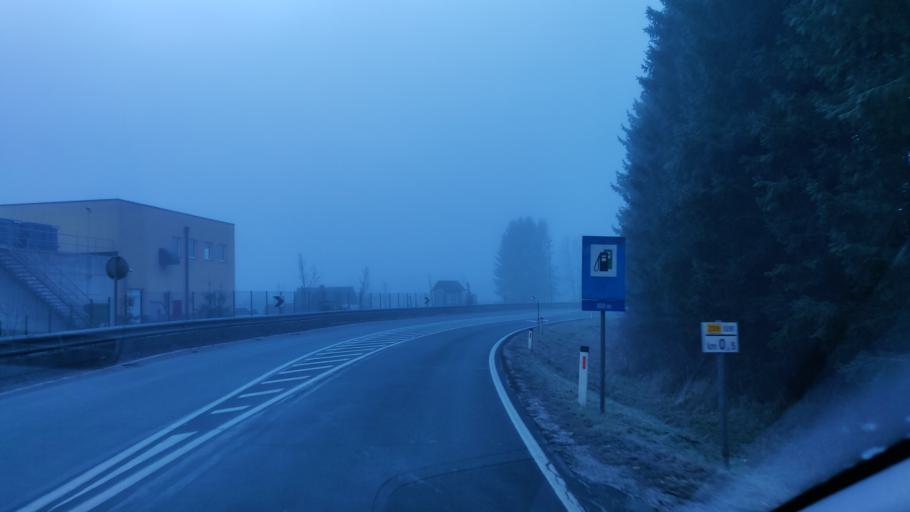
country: SI
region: Bohinj
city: Bohinjska Bistrica
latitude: 46.2791
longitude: 13.9529
